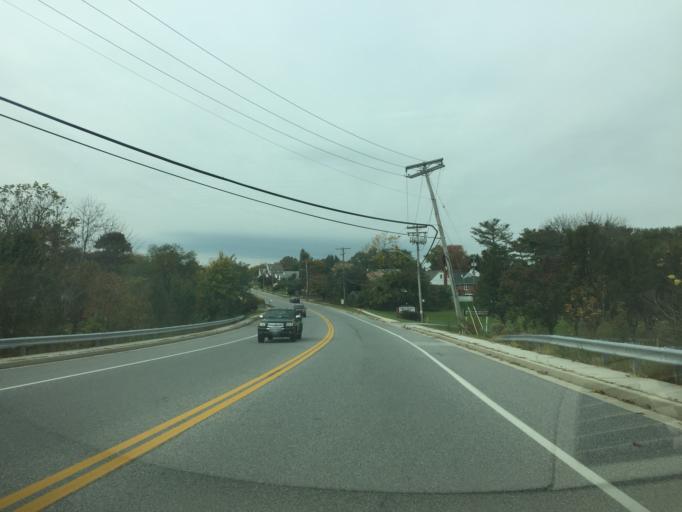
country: US
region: Maryland
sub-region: Baltimore County
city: Rosedale
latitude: 39.3417
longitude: -76.5149
